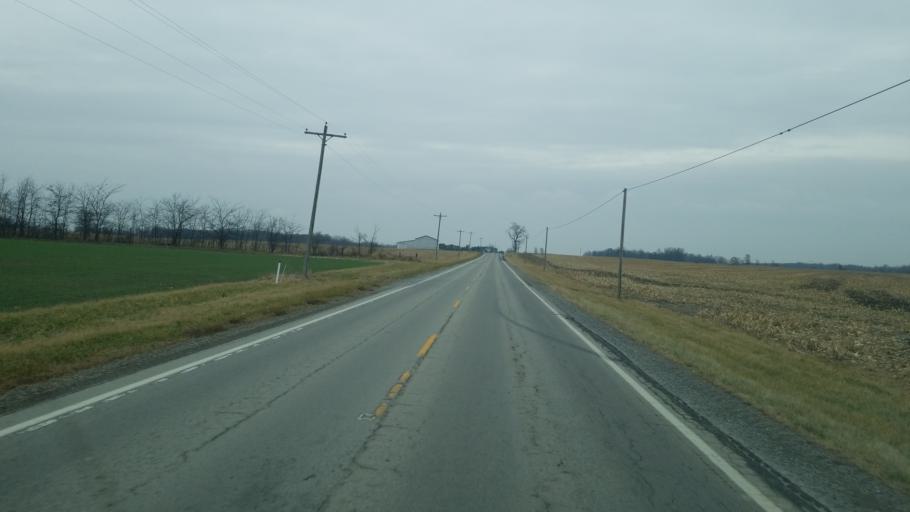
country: US
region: Ohio
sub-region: Hardin County
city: Forest
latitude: 40.7101
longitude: -83.3849
